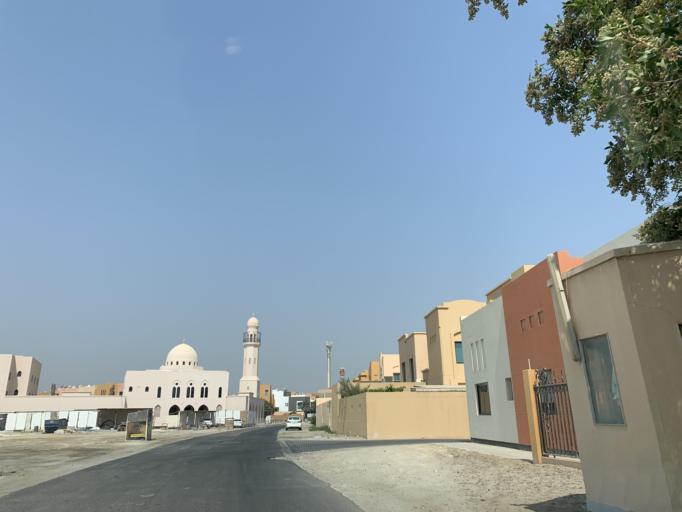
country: BH
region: Manama
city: Jidd Hafs
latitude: 26.2102
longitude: 50.5240
